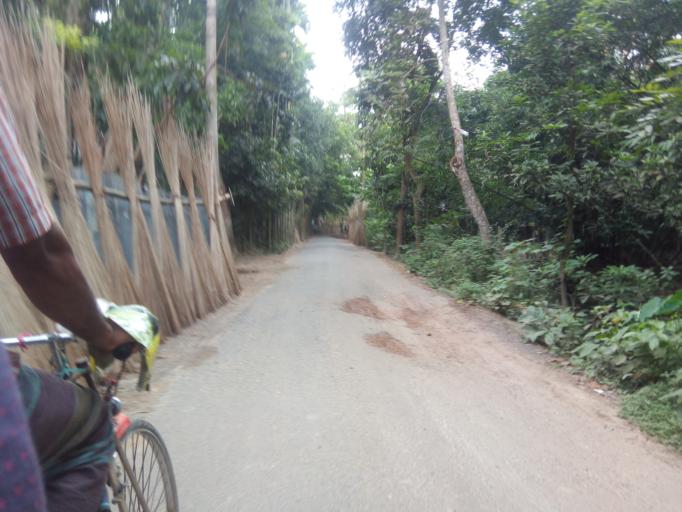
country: BD
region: Khulna
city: Kalia
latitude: 23.2157
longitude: 89.7057
